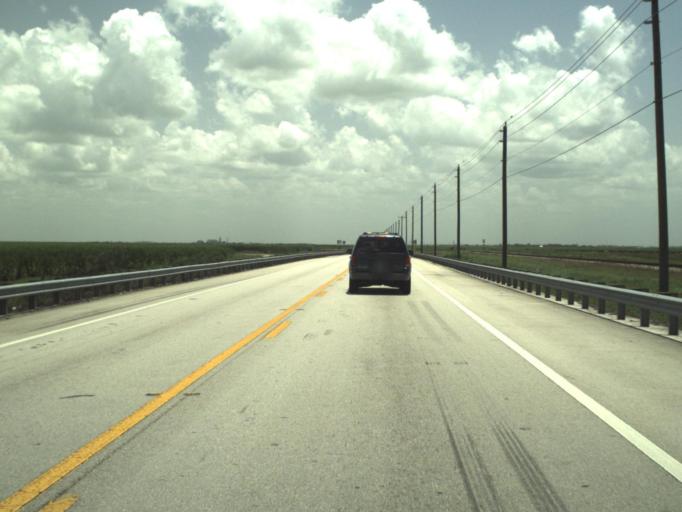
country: US
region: Florida
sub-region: Palm Beach County
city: Pahokee
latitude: 26.7669
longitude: -80.6598
